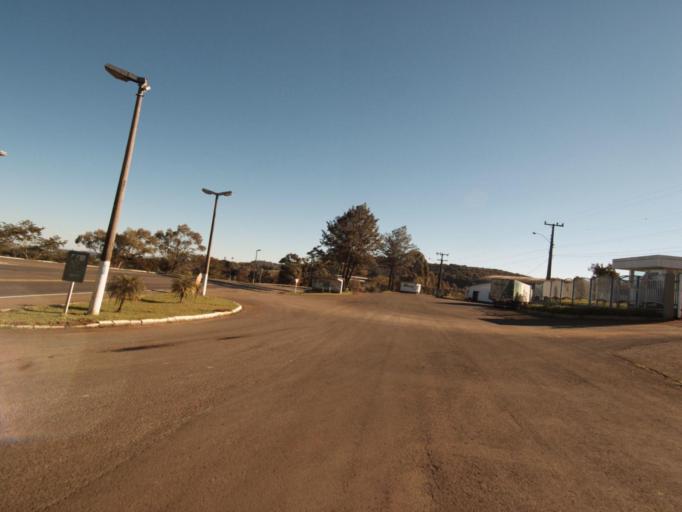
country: BR
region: Santa Catarina
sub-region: Chapeco
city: Chapeco
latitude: -26.9864
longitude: -52.6053
